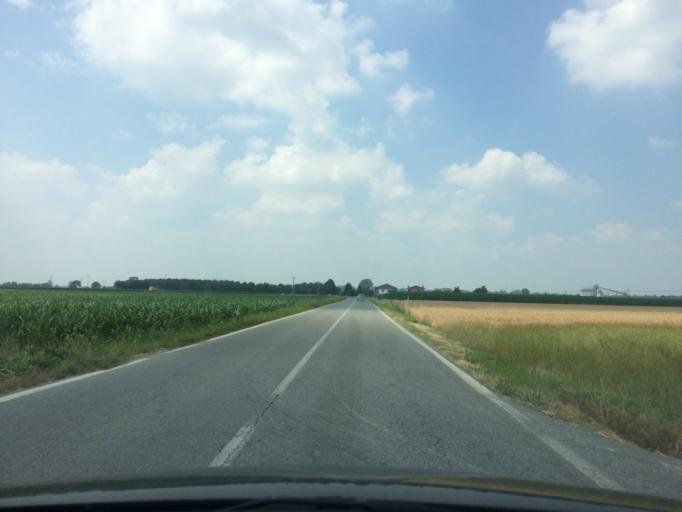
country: IT
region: Piedmont
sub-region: Provincia di Cuneo
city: Caramagna Piemonte
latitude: 44.7793
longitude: 7.7323
